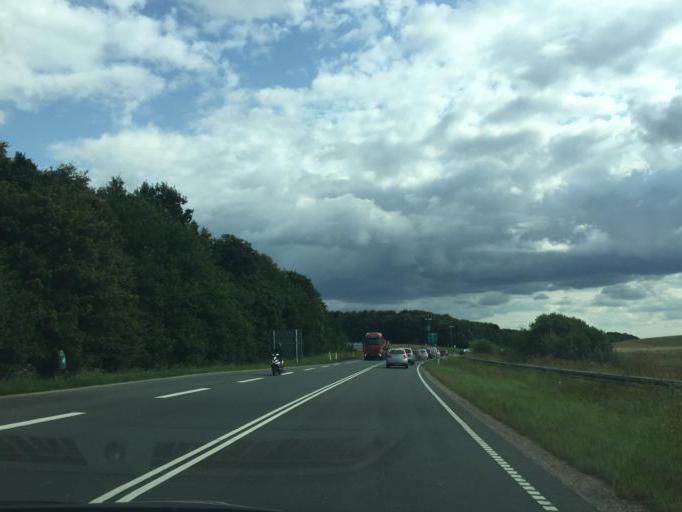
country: DK
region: Central Jutland
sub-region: Horsens Kommune
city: Horsens
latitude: 55.9122
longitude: 9.8282
